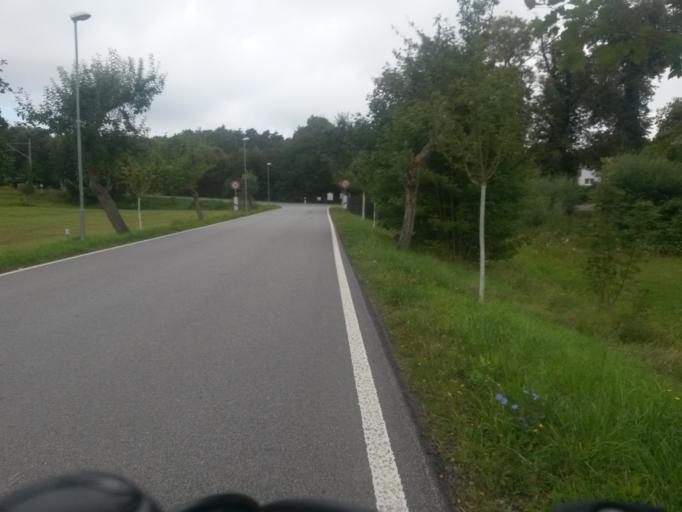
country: DE
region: Brandenburg
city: Angermunde
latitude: 53.0527
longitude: 13.9431
